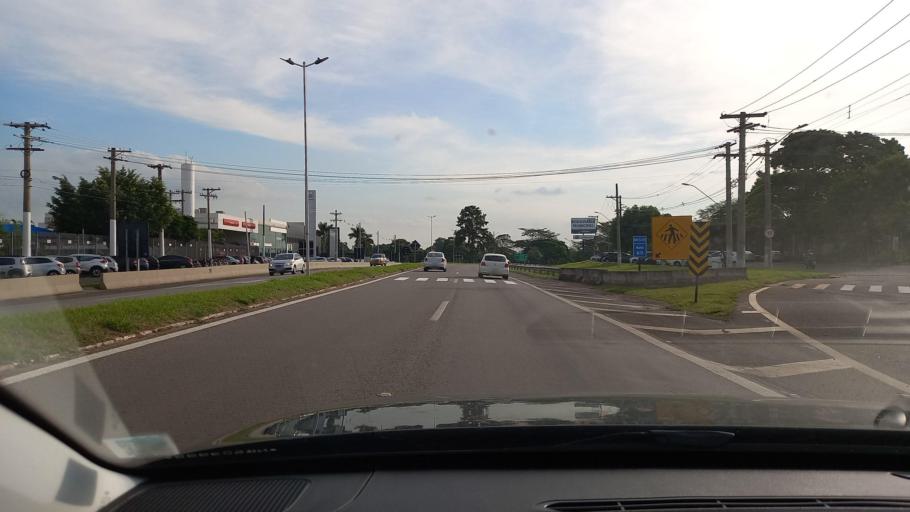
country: BR
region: Sao Paulo
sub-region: Mogi-Mirim
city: Mogi Mirim
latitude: -22.4479
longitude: -46.9796
